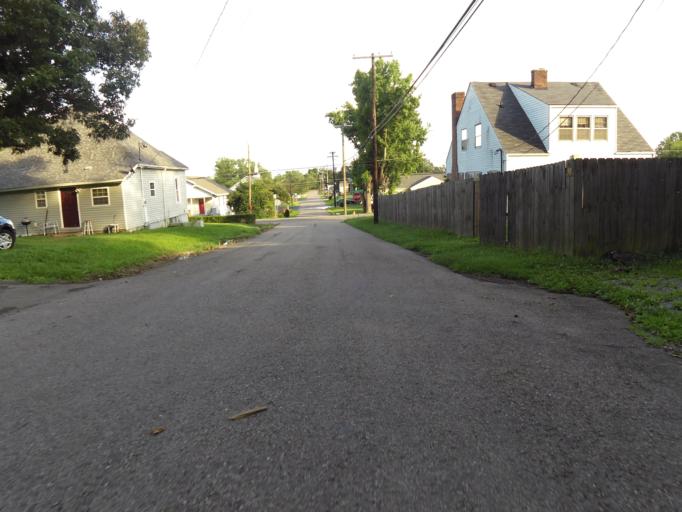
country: US
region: Tennessee
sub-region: Knox County
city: Knoxville
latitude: 35.9989
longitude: -83.9423
